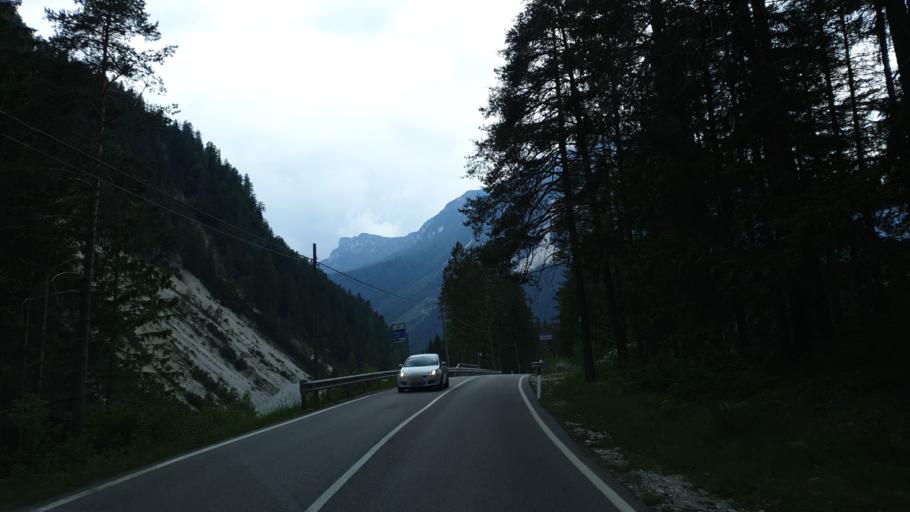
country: IT
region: Veneto
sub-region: Provincia di Belluno
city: Auronzo
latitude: 46.5771
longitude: 12.3769
